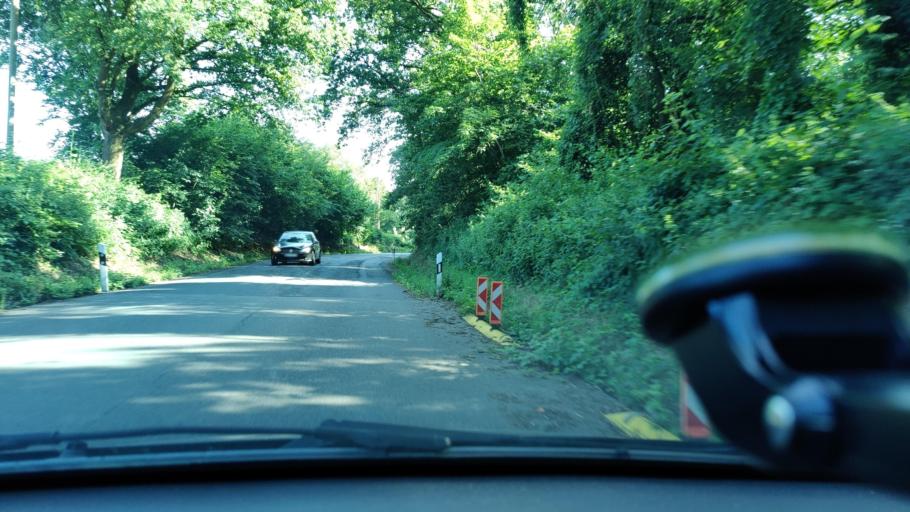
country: DE
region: North Rhine-Westphalia
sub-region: Regierungsbezirk Dusseldorf
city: Kamp-Lintfort
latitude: 51.5277
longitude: 6.5133
